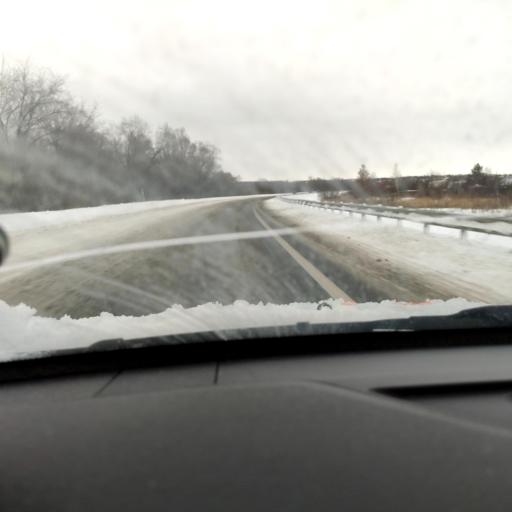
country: RU
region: Samara
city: Novosemeykino
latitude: 53.4165
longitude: 50.3349
